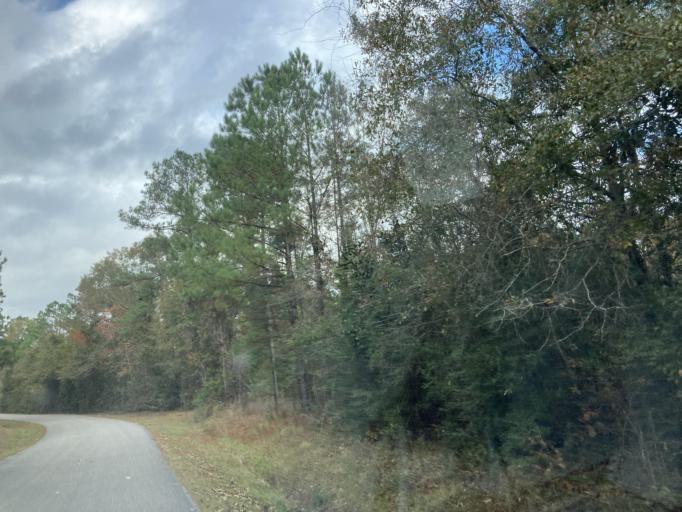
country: US
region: Mississippi
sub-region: Lamar County
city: Purvis
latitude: 31.1502
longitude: -89.5511
